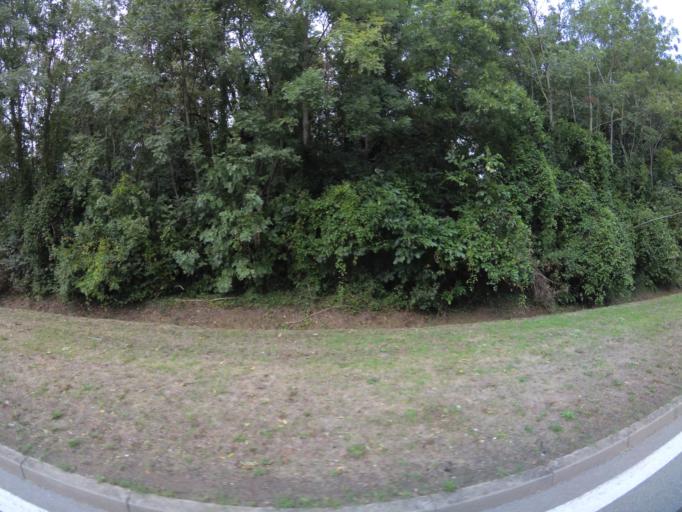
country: FR
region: Ile-de-France
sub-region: Departement de Seine-et-Marne
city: Chessy
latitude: 48.8746
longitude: 2.7702
